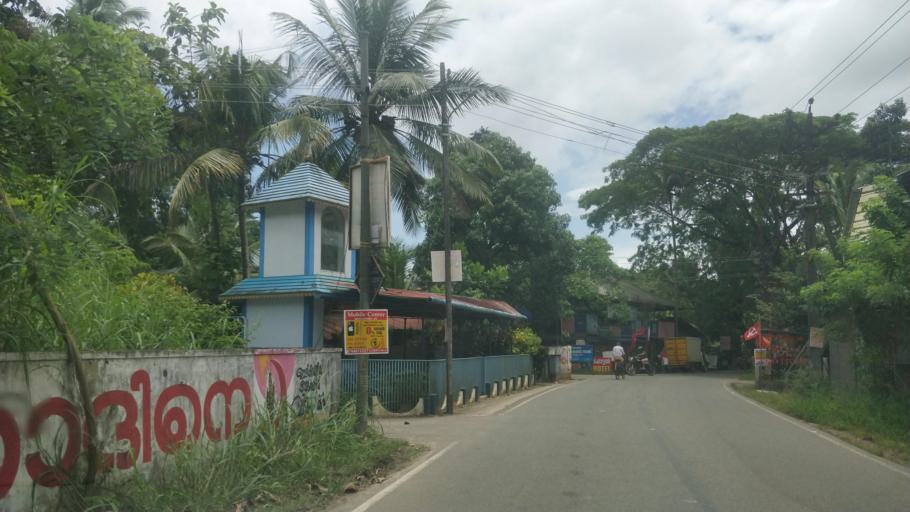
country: IN
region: Kerala
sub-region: Alappuzha
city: Shertallai
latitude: 9.6580
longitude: 76.3625
